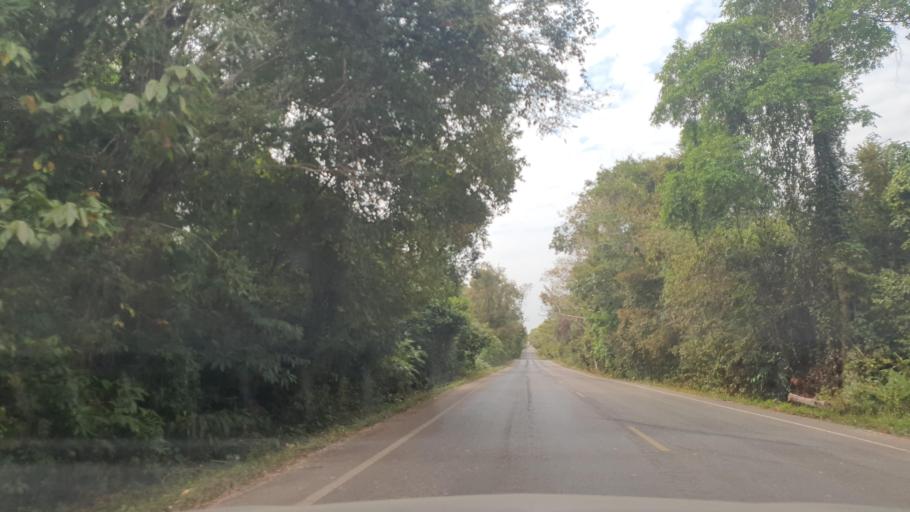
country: TH
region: Changwat Bueng Kan
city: Bung Khla
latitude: 18.2961
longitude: 103.9320
